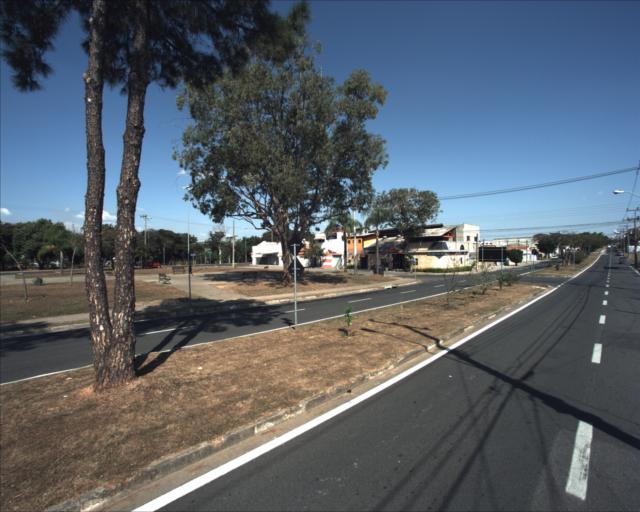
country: BR
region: Sao Paulo
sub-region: Sorocaba
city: Sorocaba
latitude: -23.4695
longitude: -47.4421
